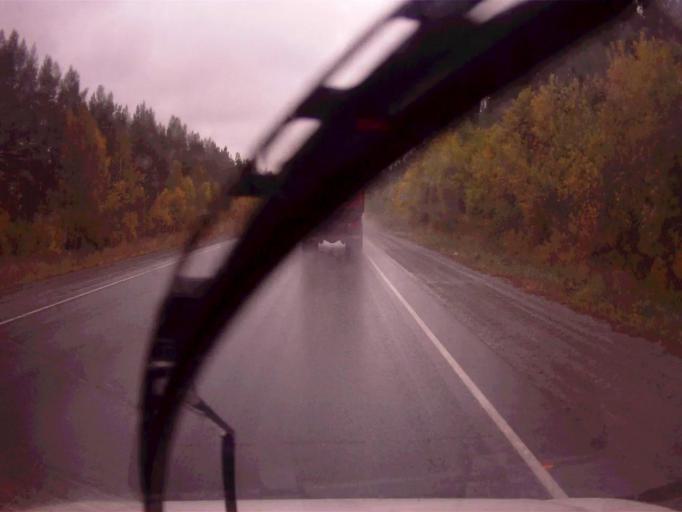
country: RU
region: Chelyabinsk
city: Roshchino
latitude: 55.3585
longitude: 61.2322
